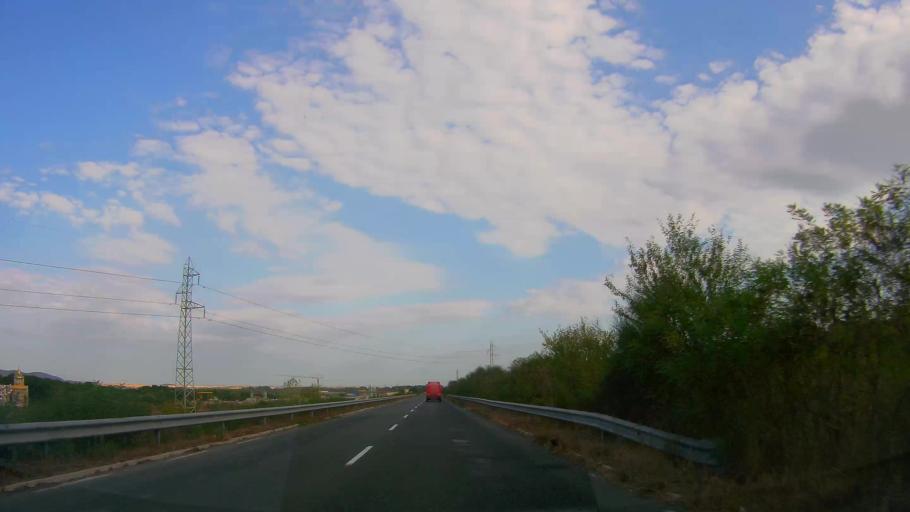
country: BG
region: Burgas
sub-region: Obshtina Sozopol
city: Sozopol
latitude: 42.3909
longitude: 27.6772
